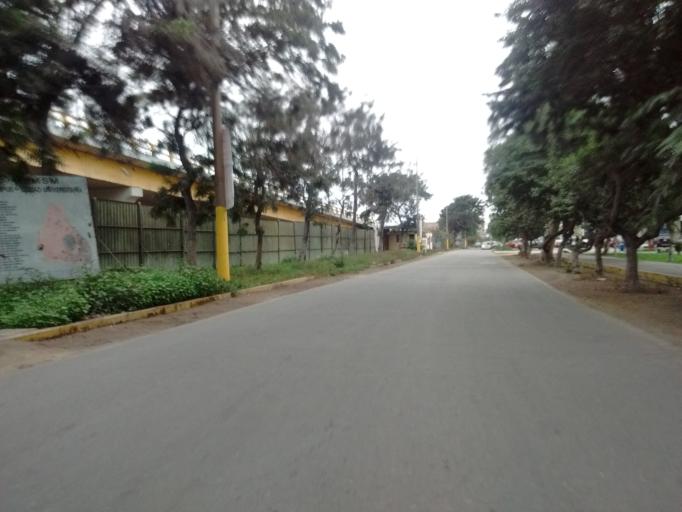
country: PE
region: Callao
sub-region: Callao
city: Callao
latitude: -12.0601
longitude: -77.0799
